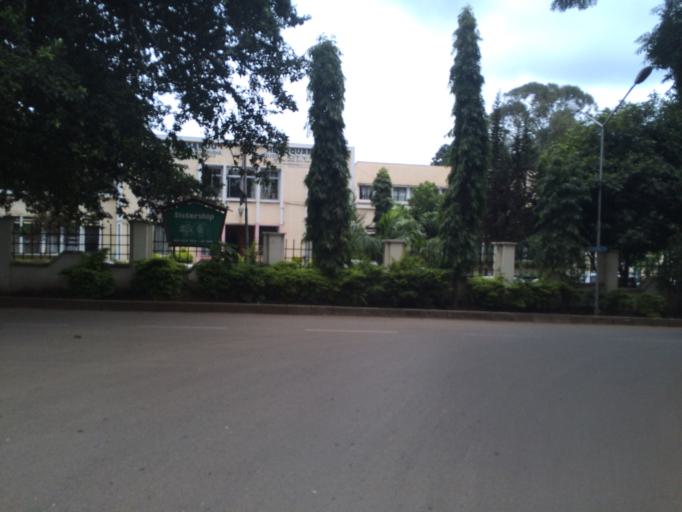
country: TZ
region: Arusha
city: Arusha
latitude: -3.3703
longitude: 36.6954
